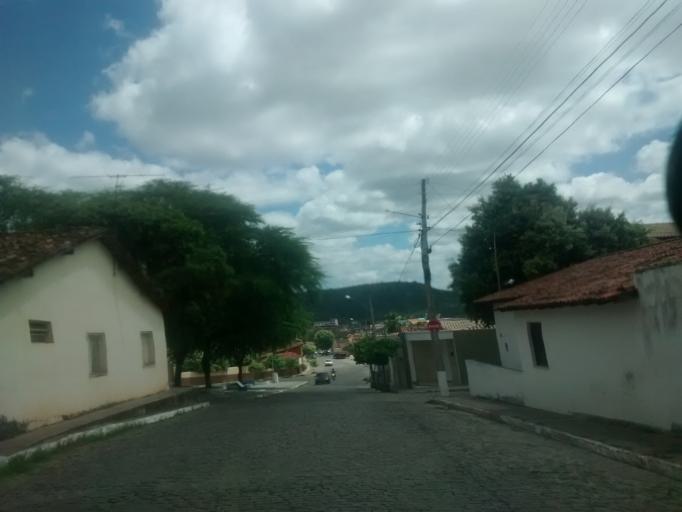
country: BR
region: Bahia
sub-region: Brumado
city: Brumado
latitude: -14.2017
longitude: -41.6697
